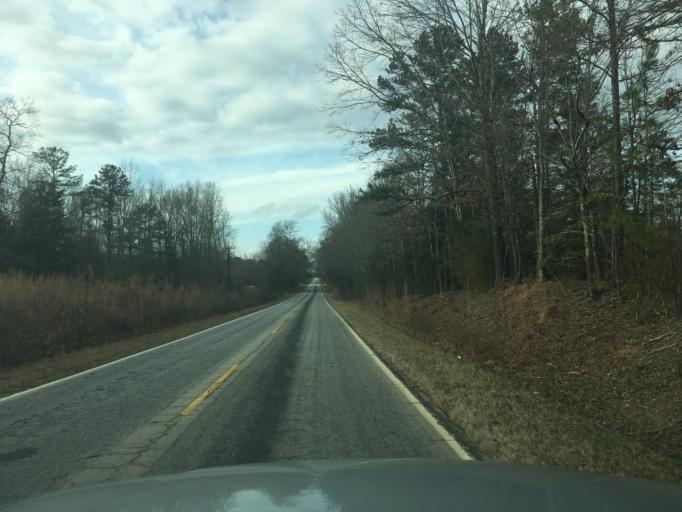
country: US
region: South Carolina
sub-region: Abbeville County
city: Due West
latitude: 34.3490
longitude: -82.4996
